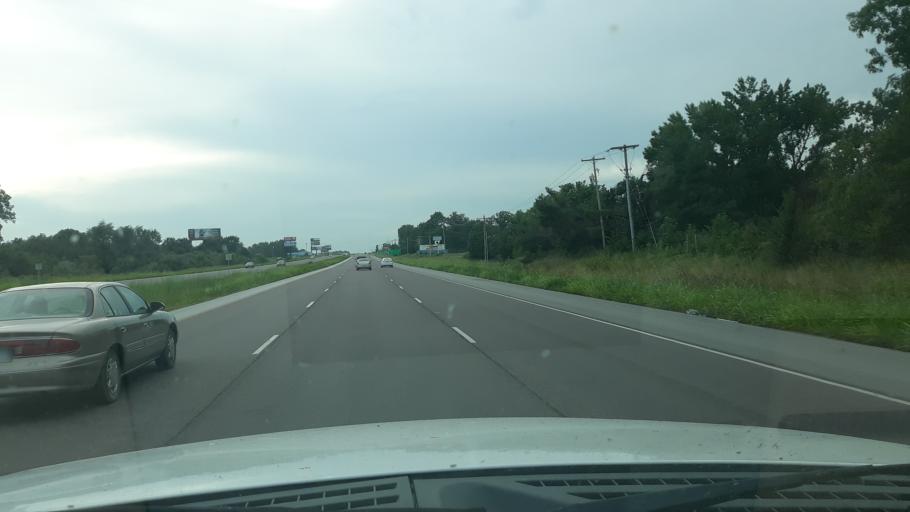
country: US
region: Illinois
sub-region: Williamson County
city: Energy
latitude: 37.7451
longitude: -89.0368
